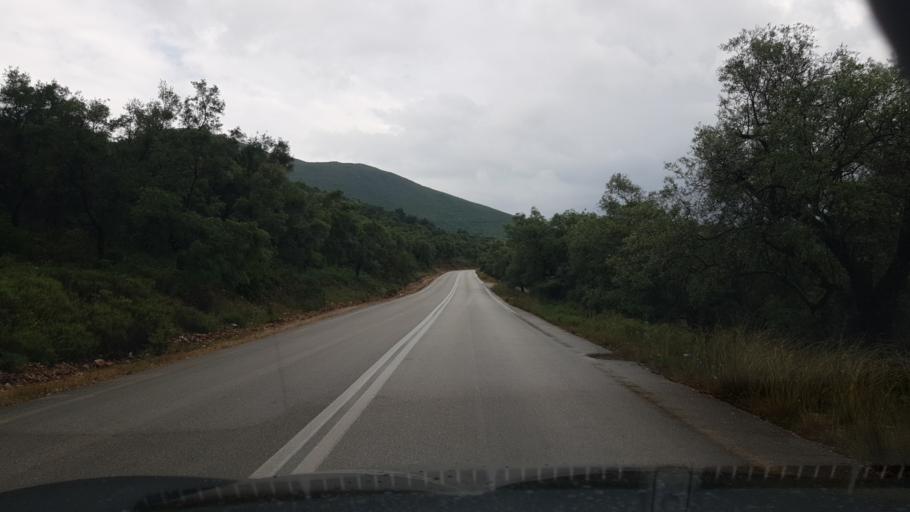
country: GR
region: Ionian Islands
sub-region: Lefkada
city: Nidri
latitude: 38.6401
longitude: 20.6751
